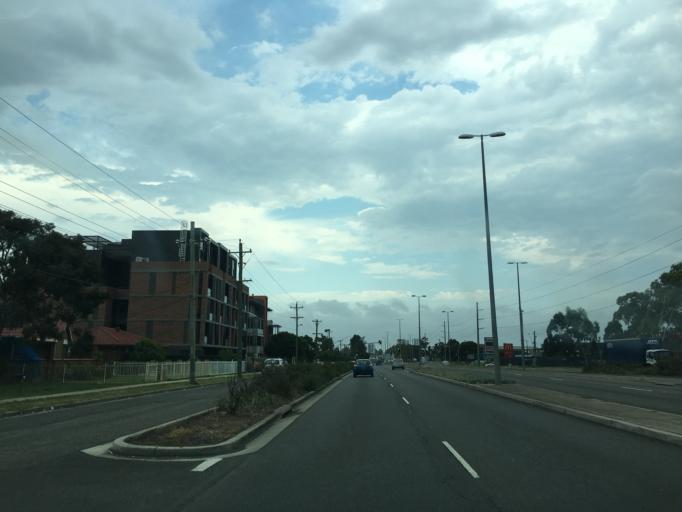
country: AU
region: New South Wales
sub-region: Liverpool
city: Miller
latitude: -33.9275
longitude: 150.8859
